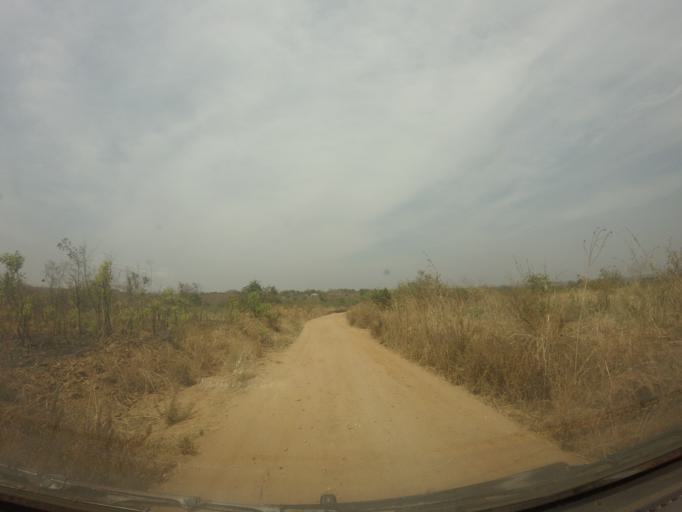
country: UG
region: Northern Region
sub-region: Zombo District
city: Zombo
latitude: 2.6826
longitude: 31.0232
